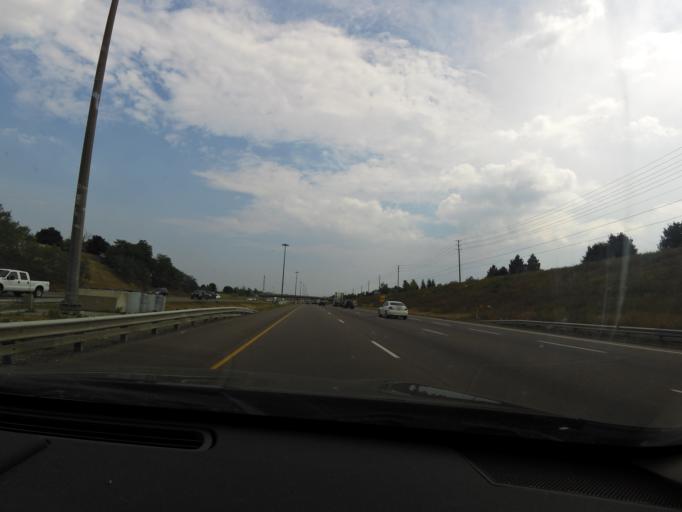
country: CA
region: Ontario
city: Brampton
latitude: 43.7209
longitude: -79.7593
